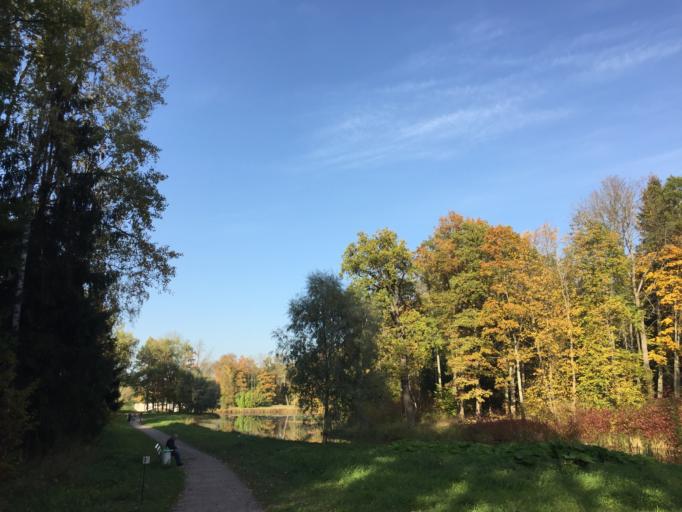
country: RU
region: St.-Petersburg
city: Pushkin
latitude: 59.7200
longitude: 30.3713
